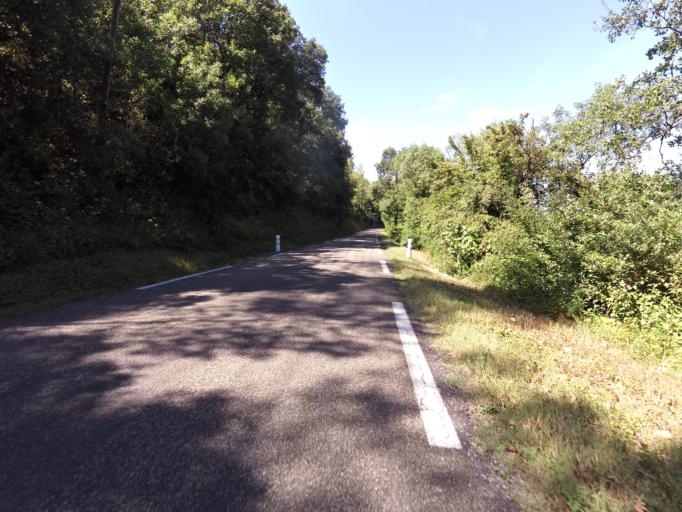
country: FR
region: Languedoc-Roussillon
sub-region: Departement du Gard
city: Sommieres
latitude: 43.8228
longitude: 4.0672
